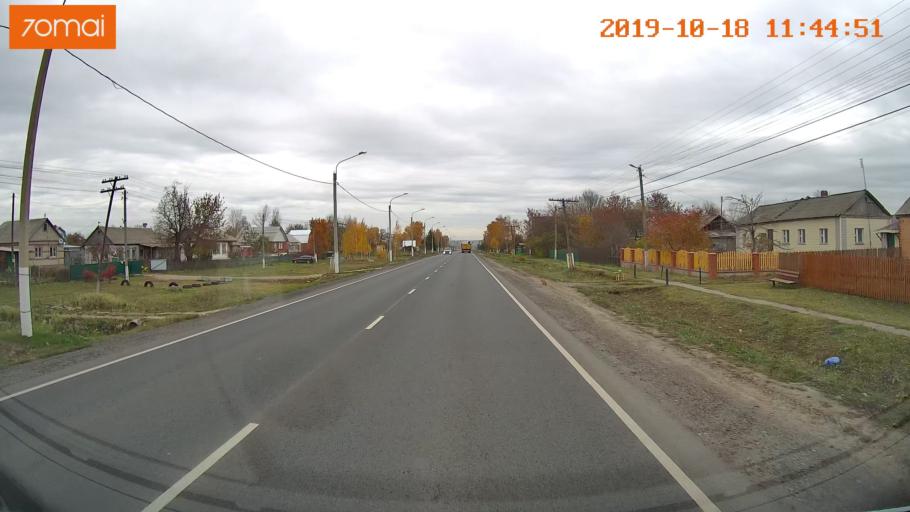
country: RU
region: Rjazan
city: Mikhaylov
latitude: 54.2057
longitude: 38.9630
